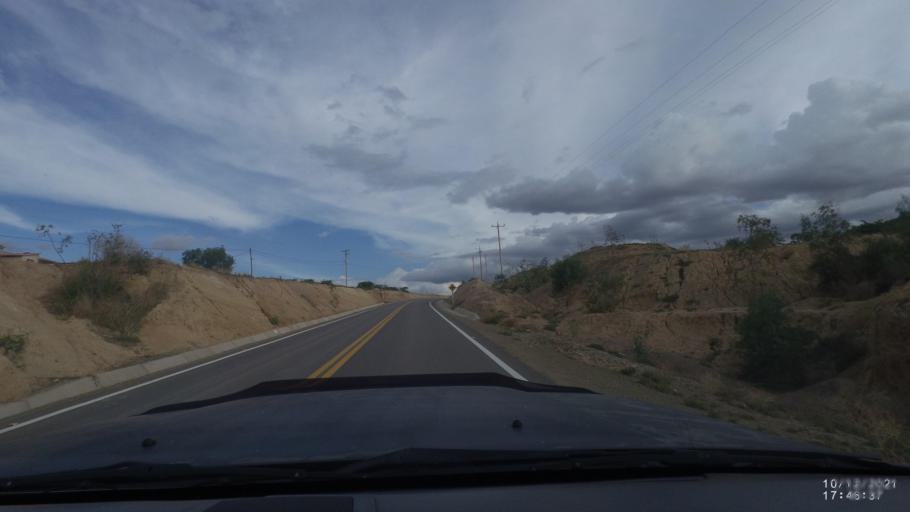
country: BO
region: Cochabamba
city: Tarata
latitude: -17.6326
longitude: -65.9927
